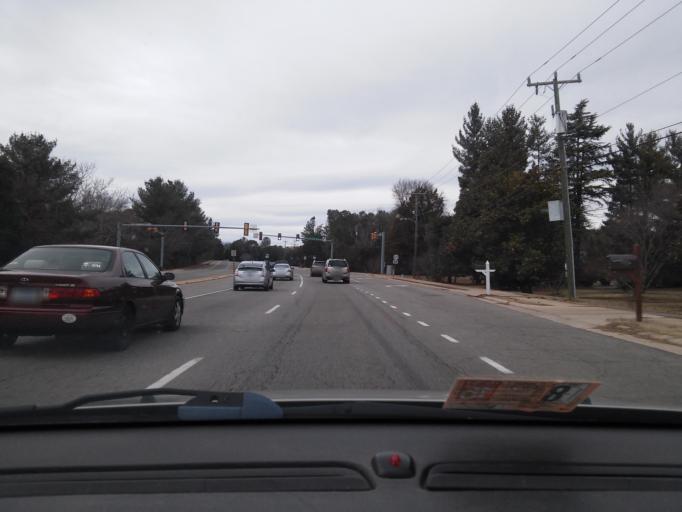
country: US
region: Virginia
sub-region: Chesterfield County
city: Bon Air
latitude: 37.5274
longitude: -77.6238
